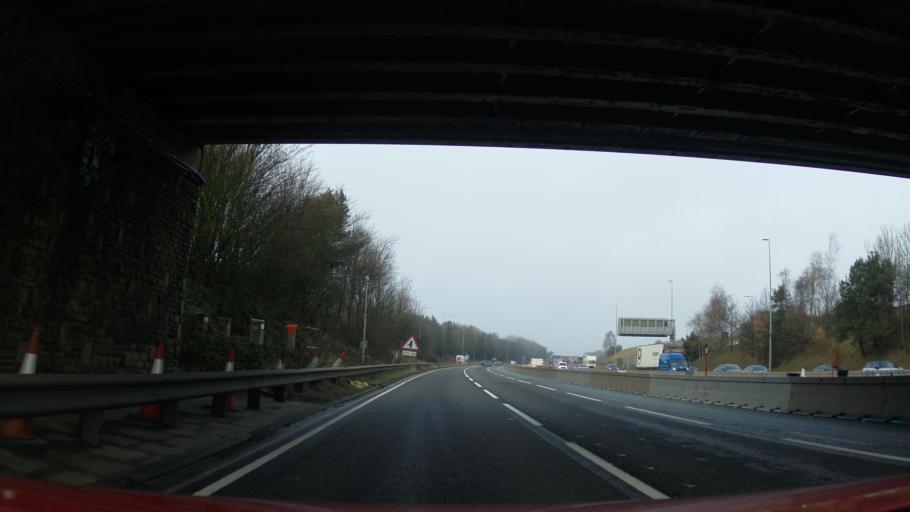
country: GB
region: England
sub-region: Warrington
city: Winwick
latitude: 53.4402
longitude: -2.5844
